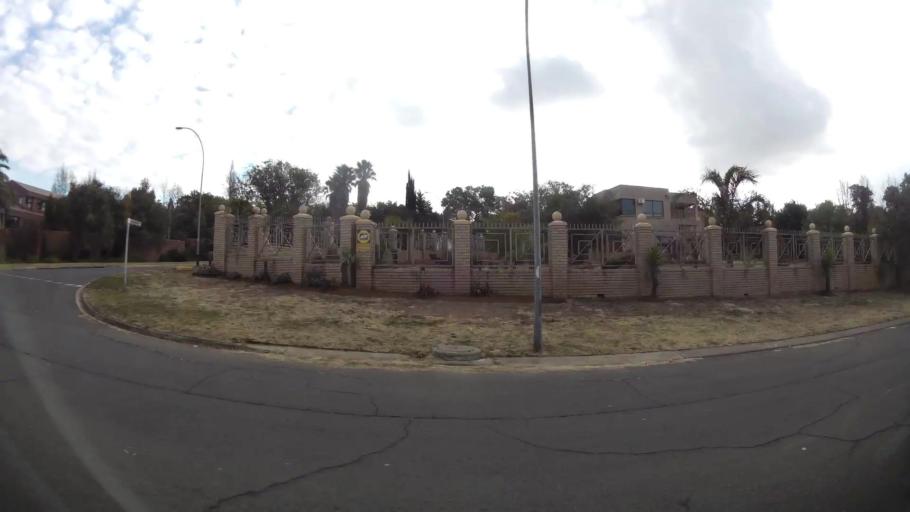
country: ZA
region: Orange Free State
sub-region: Mangaung Metropolitan Municipality
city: Bloemfontein
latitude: -29.0864
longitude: 26.2017
